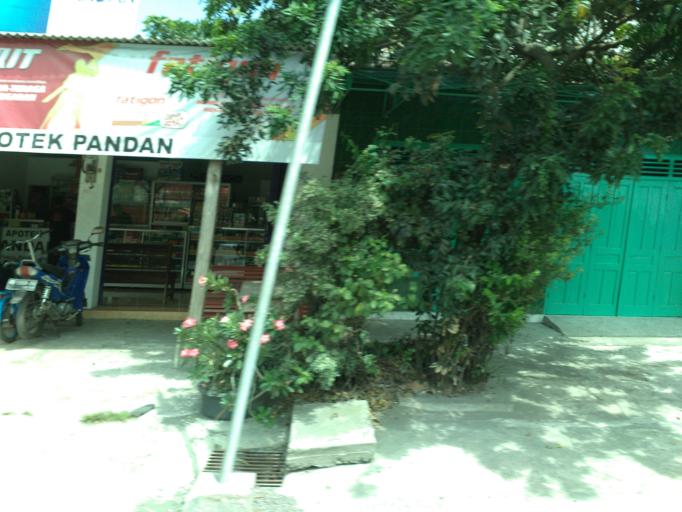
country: ID
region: Central Java
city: Jogonalan
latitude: -7.7412
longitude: 110.5322
